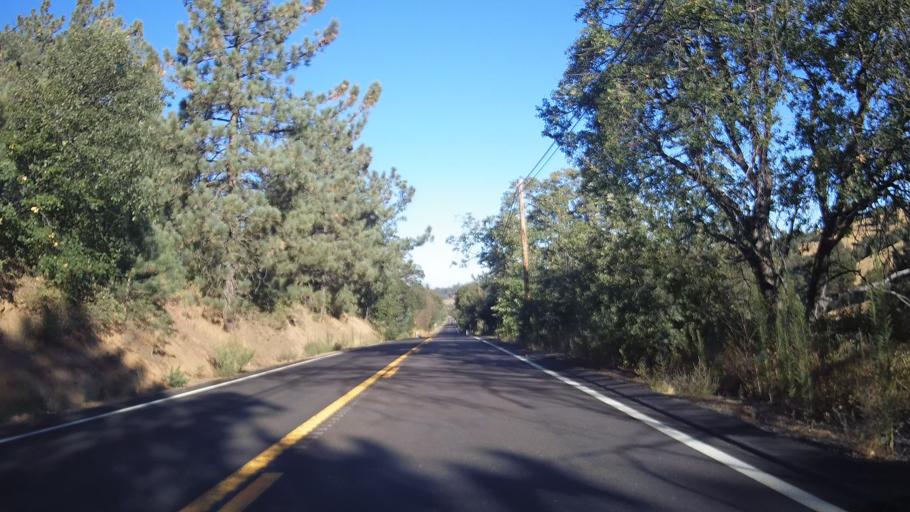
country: US
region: California
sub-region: San Diego County
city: Julian
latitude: 33.0679
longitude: -116.5871
